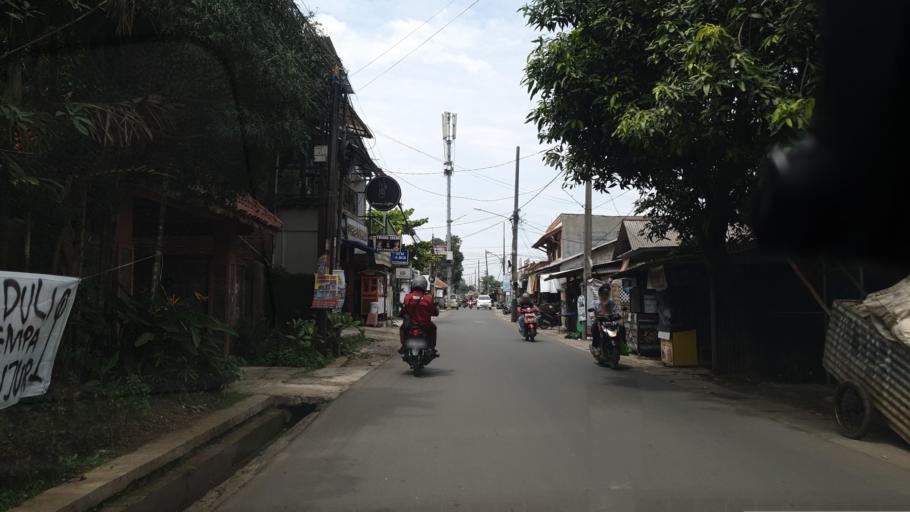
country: ID
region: West Java
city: Pamulang
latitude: -6.3679
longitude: 106.7566
